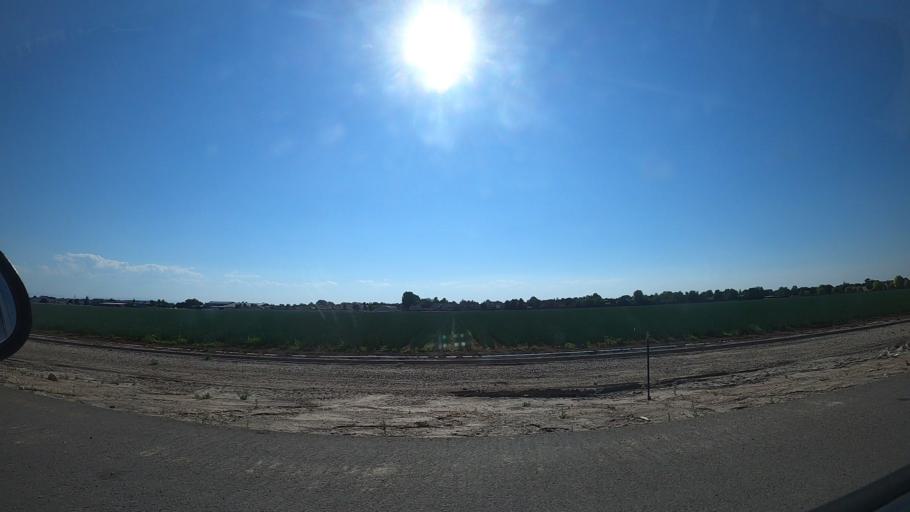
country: US
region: Idaho
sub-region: Ada County
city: Meridian
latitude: 43.6235
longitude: -116.3547
